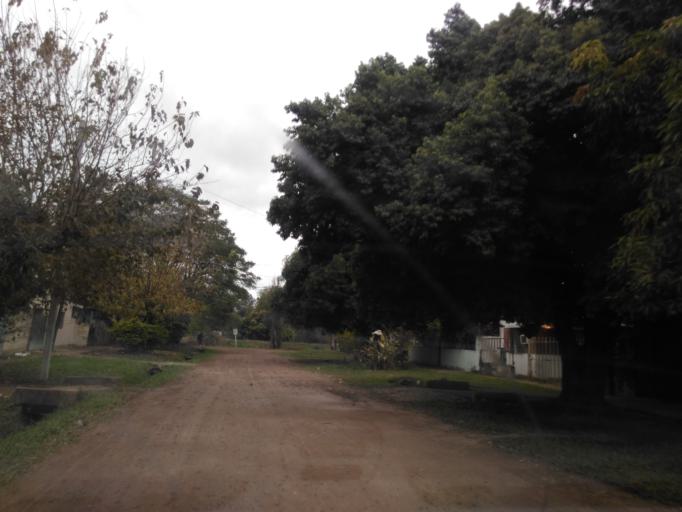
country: AR
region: Chaco
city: Fontana
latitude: -27.4350
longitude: -59.0149
